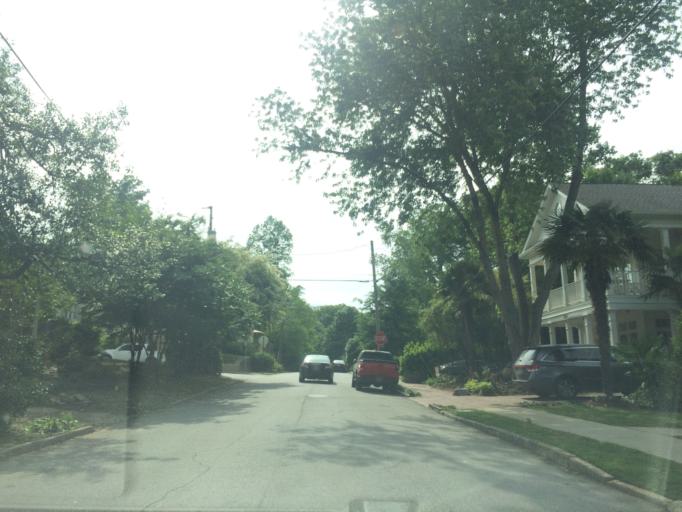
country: US
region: Georgia
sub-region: DeKalb County
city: Druid Hills
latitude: 33.7839
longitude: -84.3564
